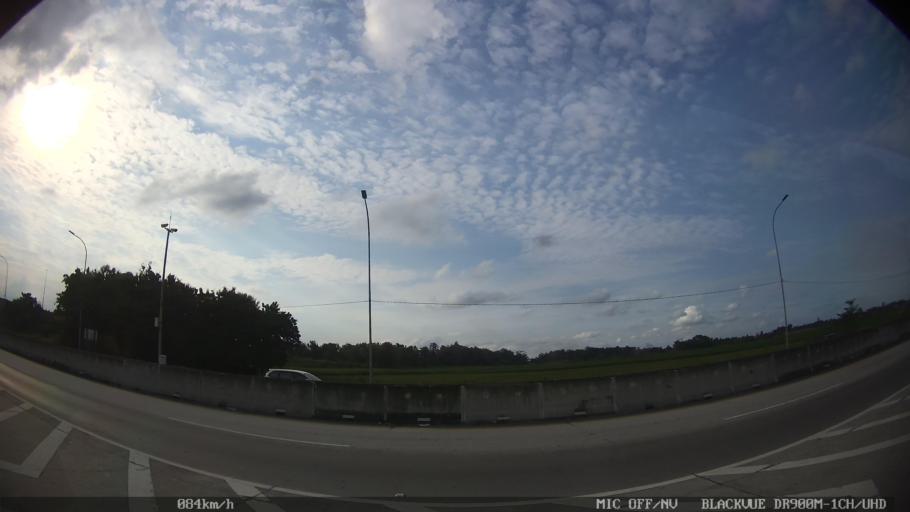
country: ID
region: North Sumatra
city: Medan
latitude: 3.6396
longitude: 98.6446
